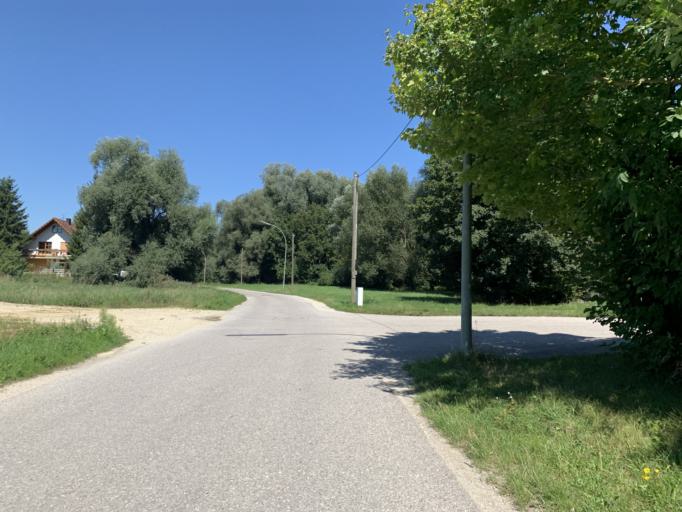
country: DE
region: Bavaria
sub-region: Upper Bavaria
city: Freising
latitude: 48.3933
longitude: 11.7193
